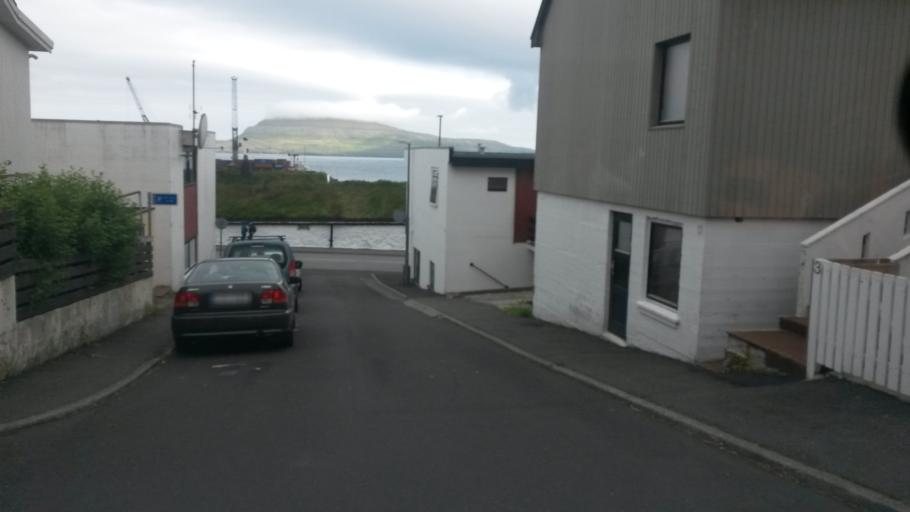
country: FO
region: Streymoy
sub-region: Torshavn
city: Torshavn
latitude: 62.0042
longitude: -6.7777
